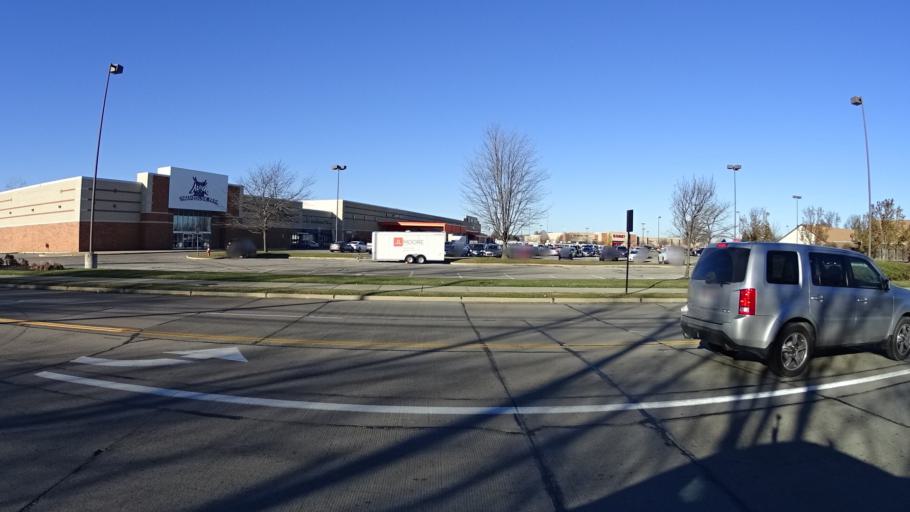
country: US
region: Ohio
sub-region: Lorain County
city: Elyria
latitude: 41.3865
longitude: -82.1046
